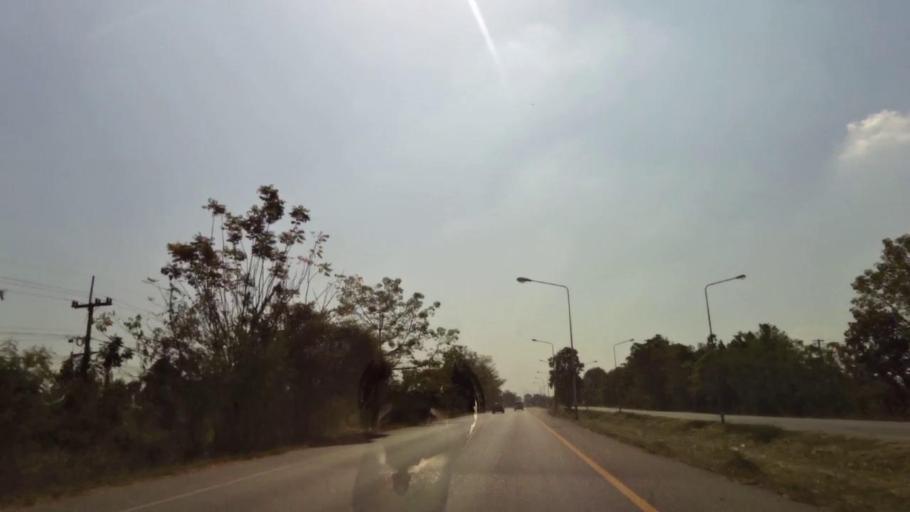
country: TH
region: Phichit
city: Wachira Barami
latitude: 16.3843
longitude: 100.1369
